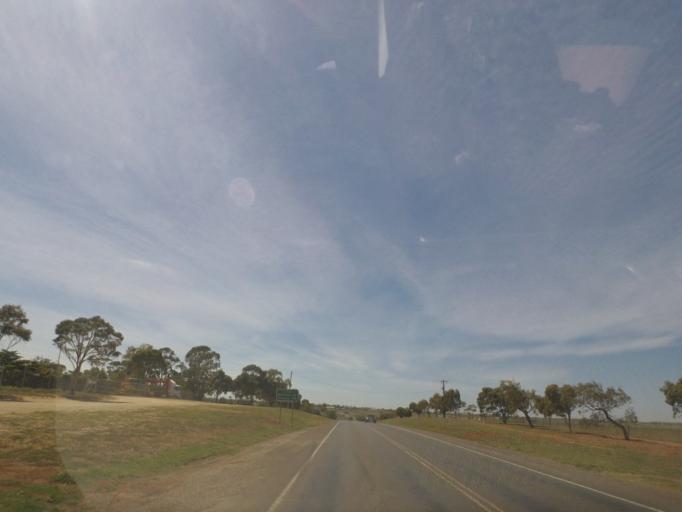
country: AU
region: Victoria
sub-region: Moorabool
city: Bacchus Marsh
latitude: -37.6938
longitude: 144.4441
